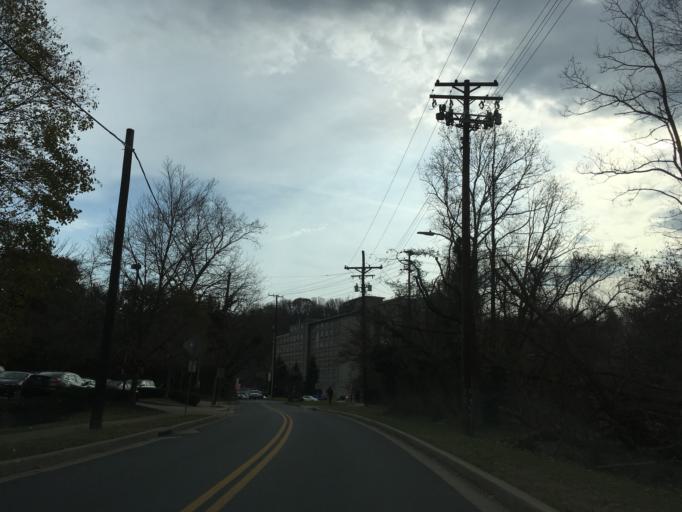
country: US
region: Maryland
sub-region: Howard County
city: Ellicott City
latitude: 39.2690
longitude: -76.7937
